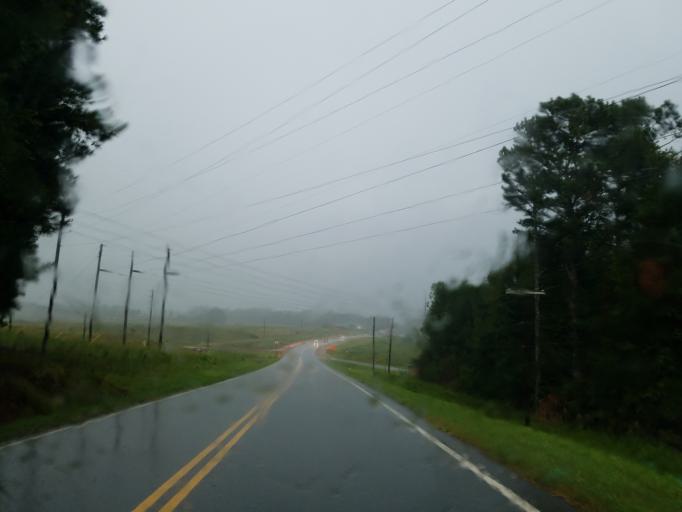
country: US
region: Georgia
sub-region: Floyd County
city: Shannon
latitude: 34.3679
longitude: -85.0574
